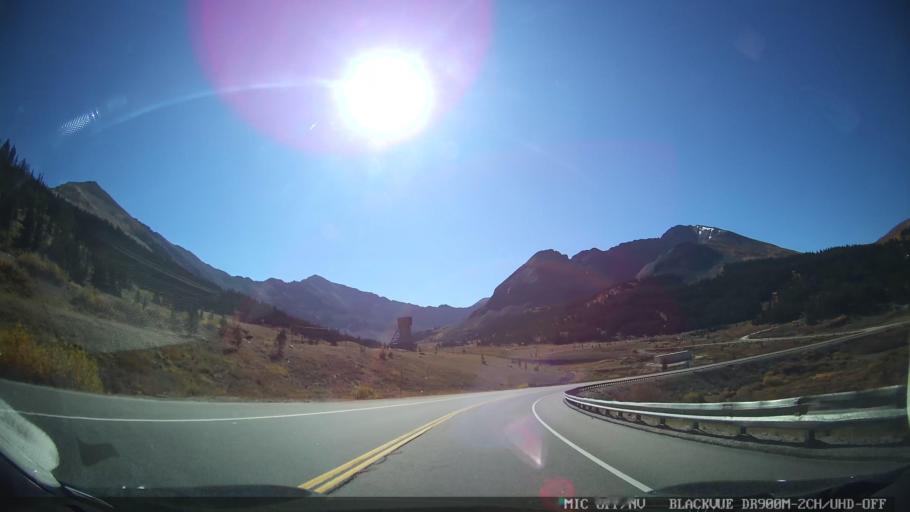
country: US
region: Colorado
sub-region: Lake County
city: Leadville
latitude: 39.3632
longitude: -106.1744
